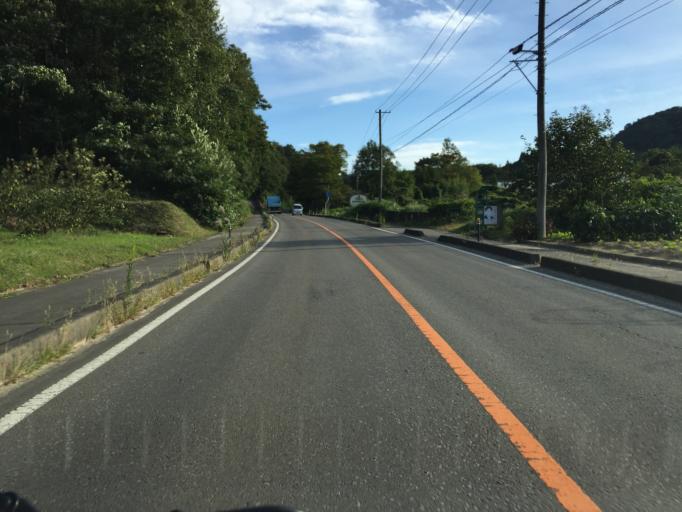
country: JP
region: Fukushima
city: Hobaramachi
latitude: 37.7623
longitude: 140.5971
